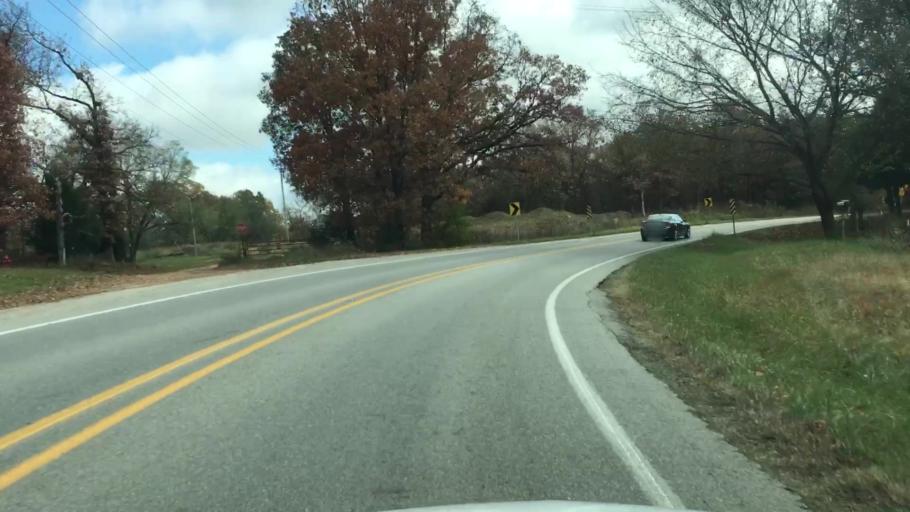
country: US
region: Arkansas
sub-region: Benton County
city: Gentry
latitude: 36.2632
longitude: -94.4522
